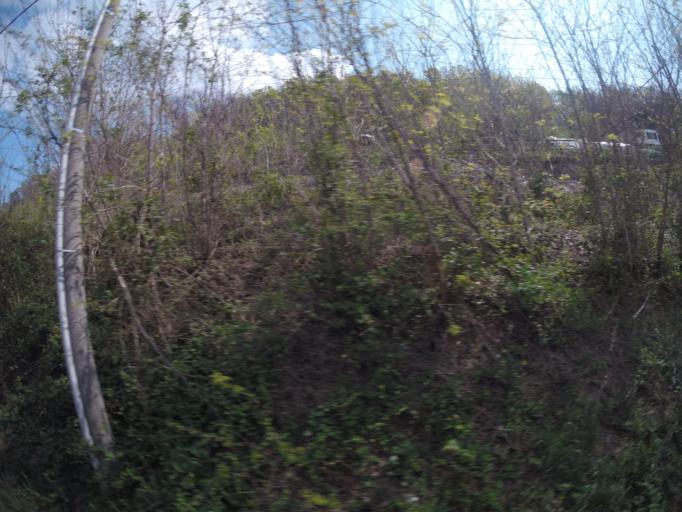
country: IT
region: Piedmont
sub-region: Provincia Verbano-Cusio-Ossola
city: Omegna
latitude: 45.8522
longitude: 8.4069
